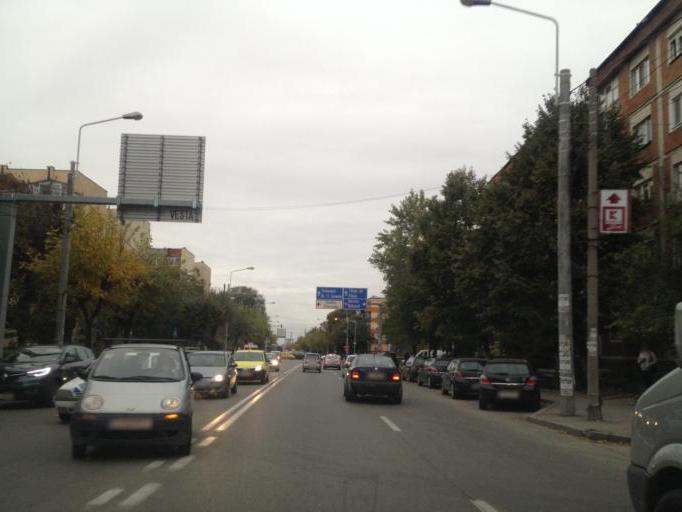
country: RO
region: Dolj
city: Craiova
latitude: 44.3285
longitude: 23.8142
